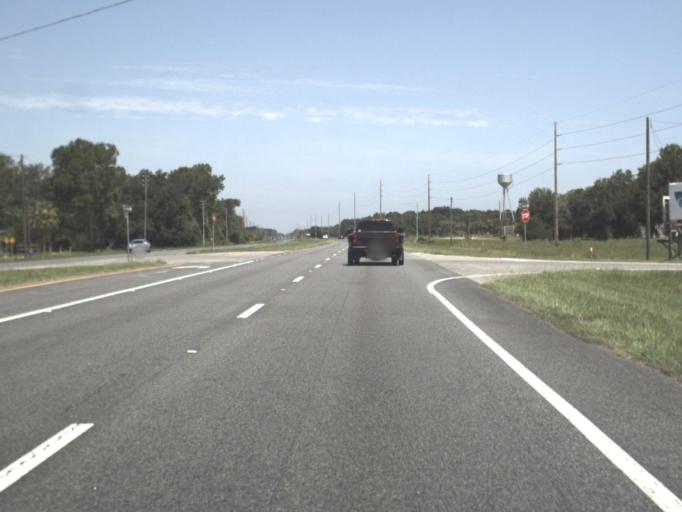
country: US
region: Florida
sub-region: Dixie County
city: Cross City
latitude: 29.6146
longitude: -83.0918
